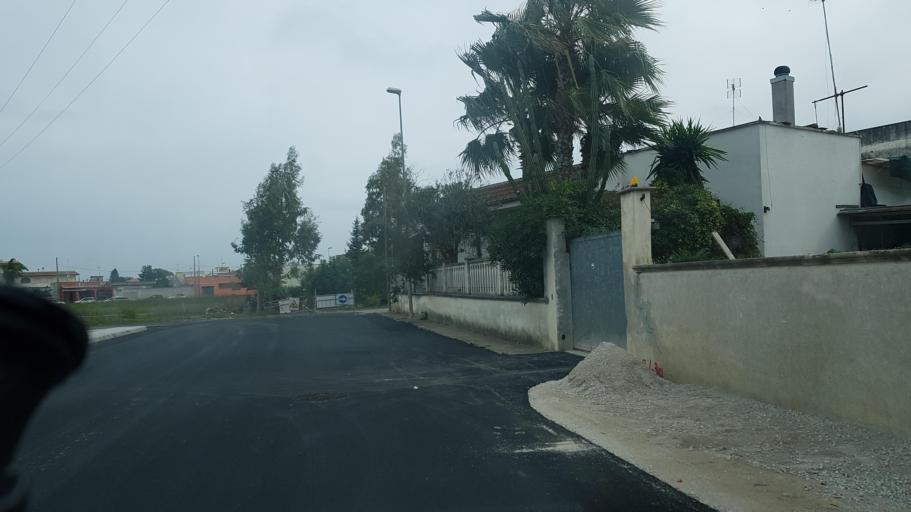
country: IT
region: Apulia
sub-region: Provincia di Brindisi
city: Cellino San Marco
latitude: 40.4767
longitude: 17.9736
